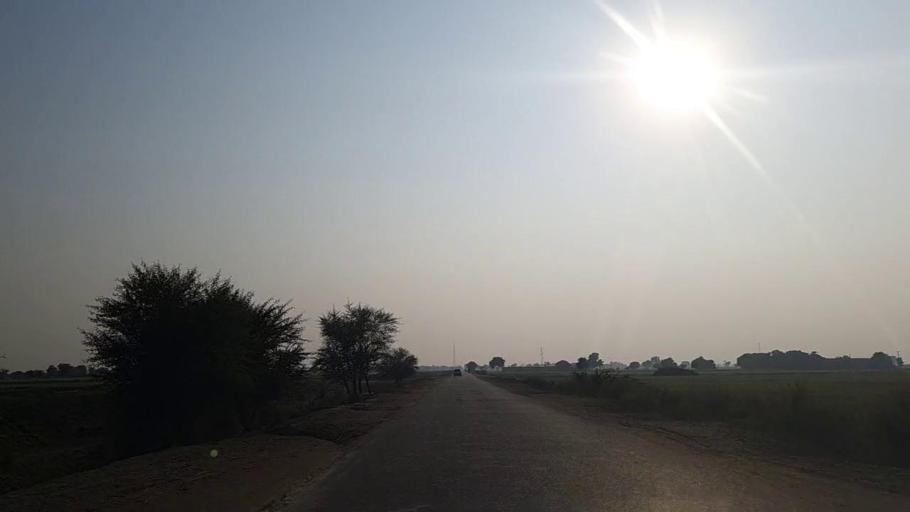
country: PK
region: Sindh
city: Shahpur Chakar
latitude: 26.2109
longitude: 68.5648
